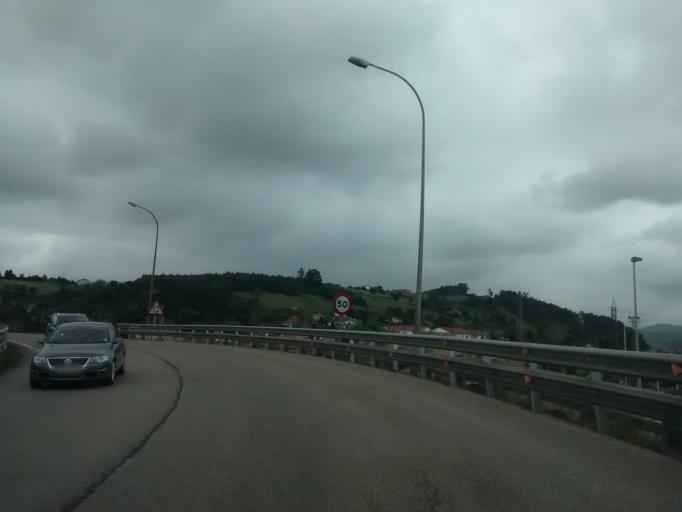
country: ES
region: Cantabria
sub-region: Provincia de Cantabria
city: Torrelavega
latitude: 43.3741
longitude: -4.0432
